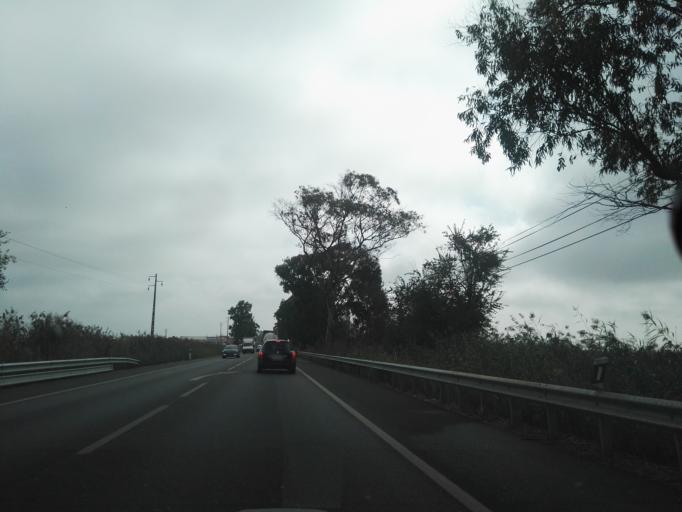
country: PT
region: Lisbon
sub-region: Vila Franca de Xira
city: Vila Franca de Xira
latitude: 38.9441
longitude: -8.9514
